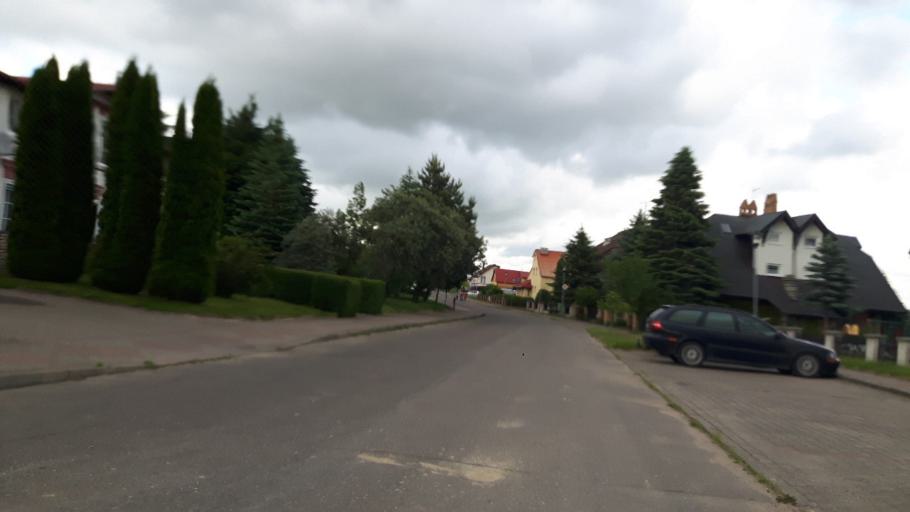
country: PL
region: West Pomeranian Voivodeship
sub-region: Powiat kolobrzeski
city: Ustronie Morskie
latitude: 54.2044
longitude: 15.7232
